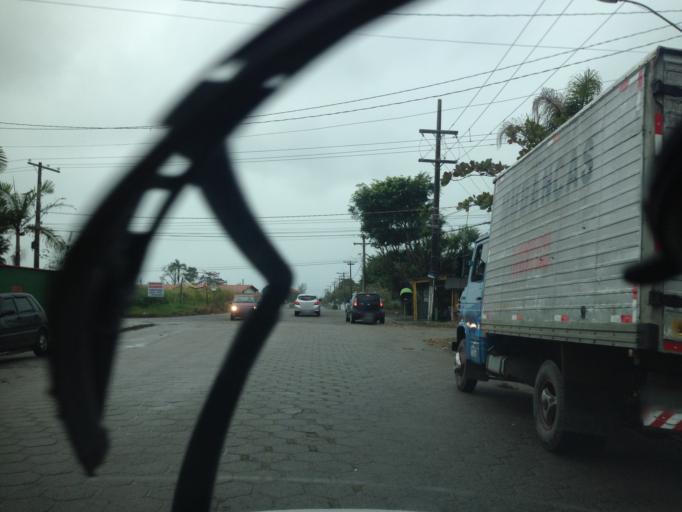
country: BR
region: Sao Paulo
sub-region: Itanhaem
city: Itanhaem
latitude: -24.2207
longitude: -46.8648
